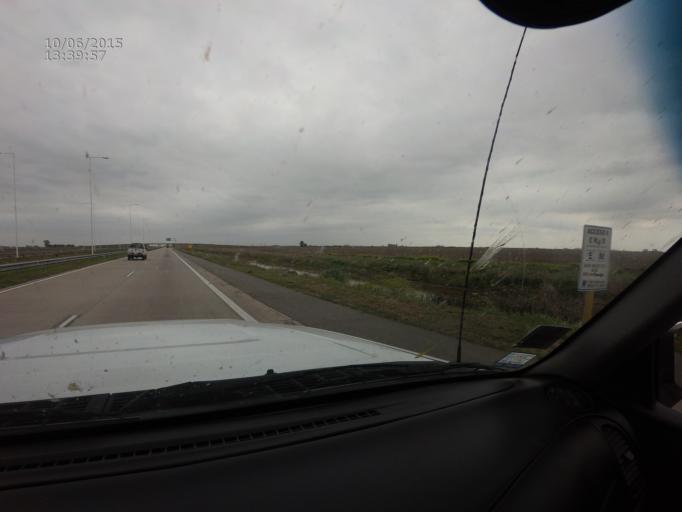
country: AR
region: Cordoba
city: Leones
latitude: -32.5981
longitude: -62.4676
